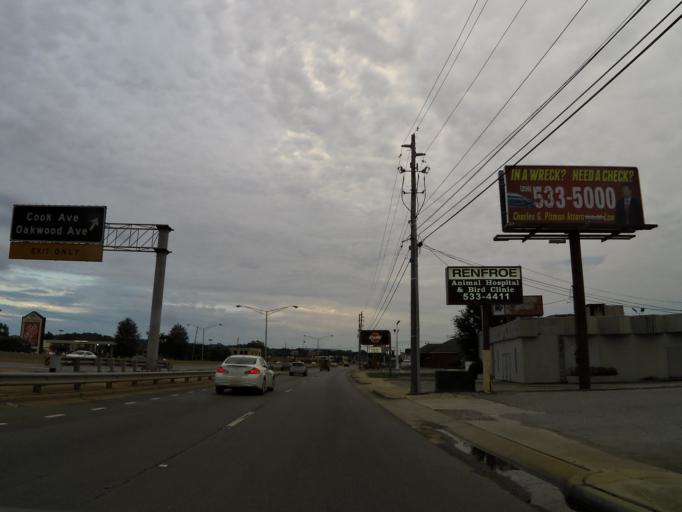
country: US
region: Alabama
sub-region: Madison County
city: Huntsville
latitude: 34.7416
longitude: -86.6004
